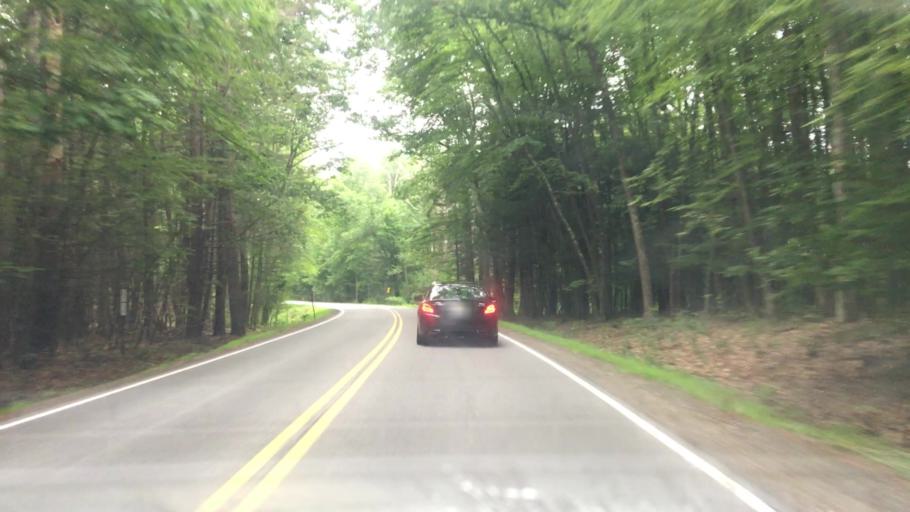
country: US
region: New Hampshire
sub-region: Rockingham County
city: Greenland
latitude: 43.0901
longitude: -70.8374
